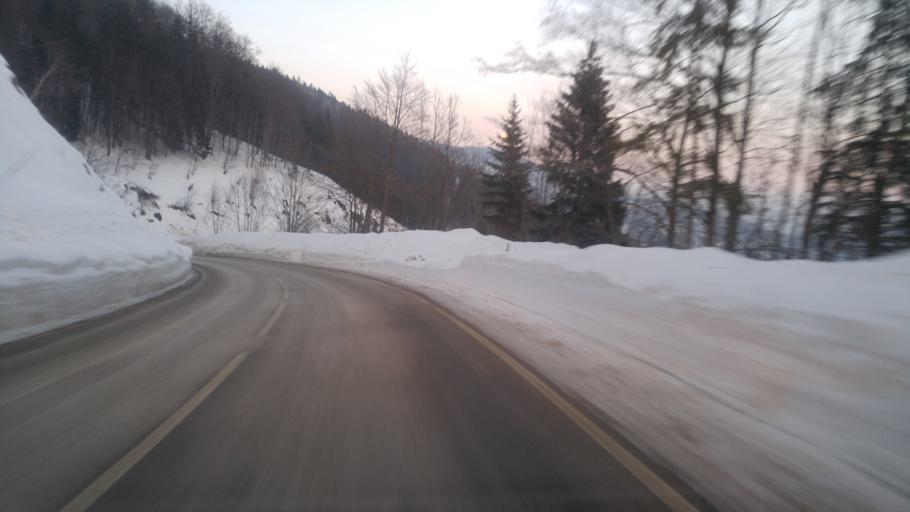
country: AT
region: Lower Austria
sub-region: Politischer Bezirk Wiener Neustadt
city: Gutenstein
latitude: 47.8754
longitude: 15.8113
